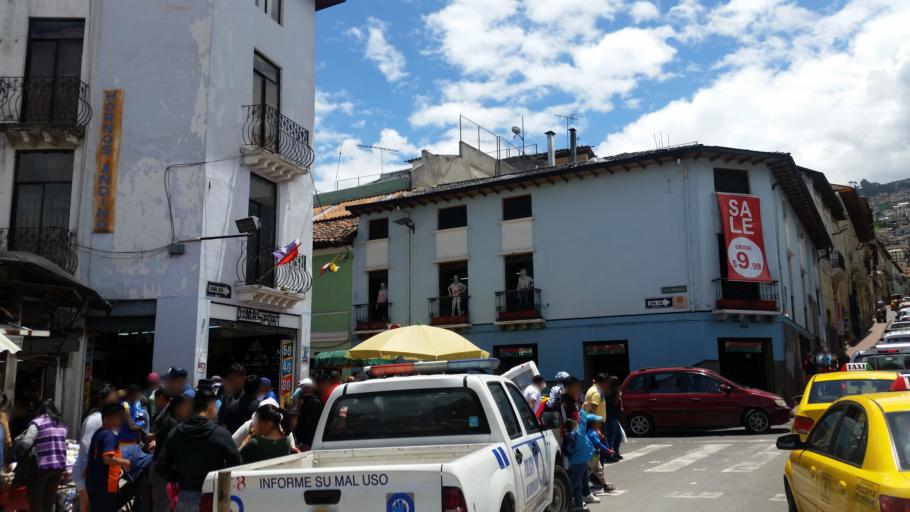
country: EC
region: Pichincha
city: Quito
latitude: -0.2175
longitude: -78.5150
